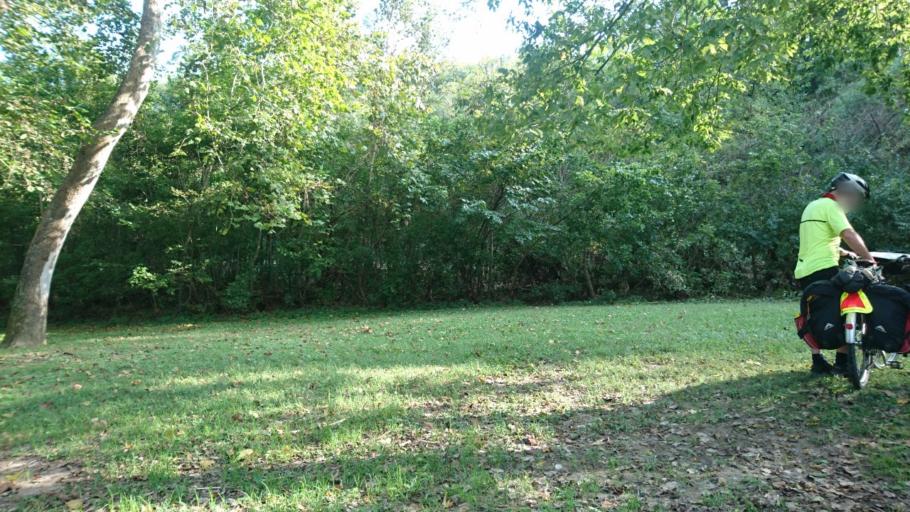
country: US
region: Missouri
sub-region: Franklin County
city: Pacific
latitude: 38.4992
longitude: -90.6914
